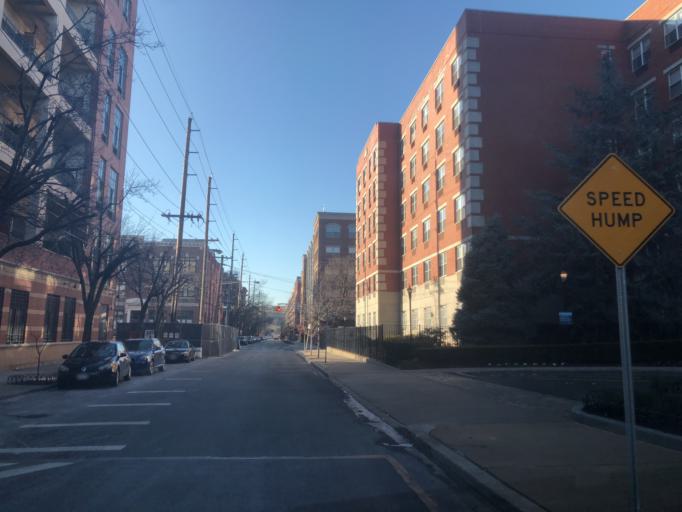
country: US
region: New Jersey
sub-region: Hudson County
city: Hoboken
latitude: 40.7289
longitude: -74.0421
